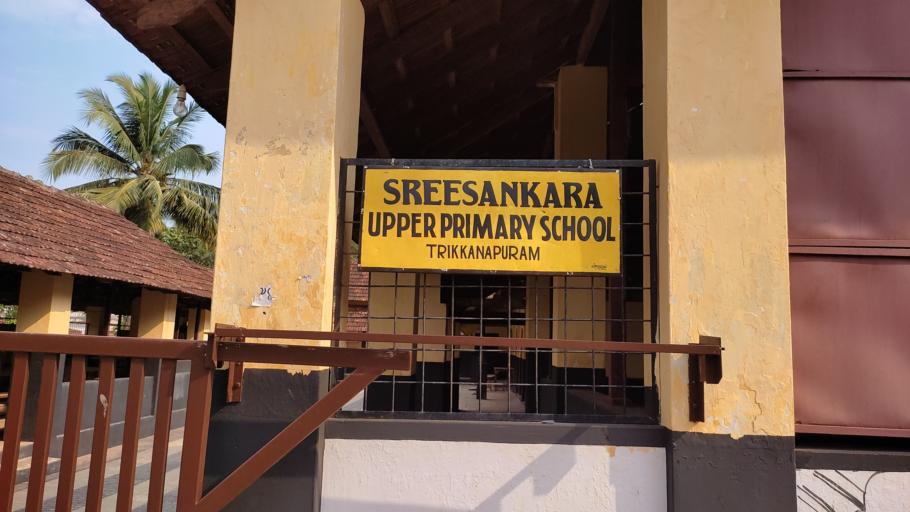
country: IN
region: Kerala
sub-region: Malappuram
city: Ponnani
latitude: 10.8390
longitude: 75.9887
